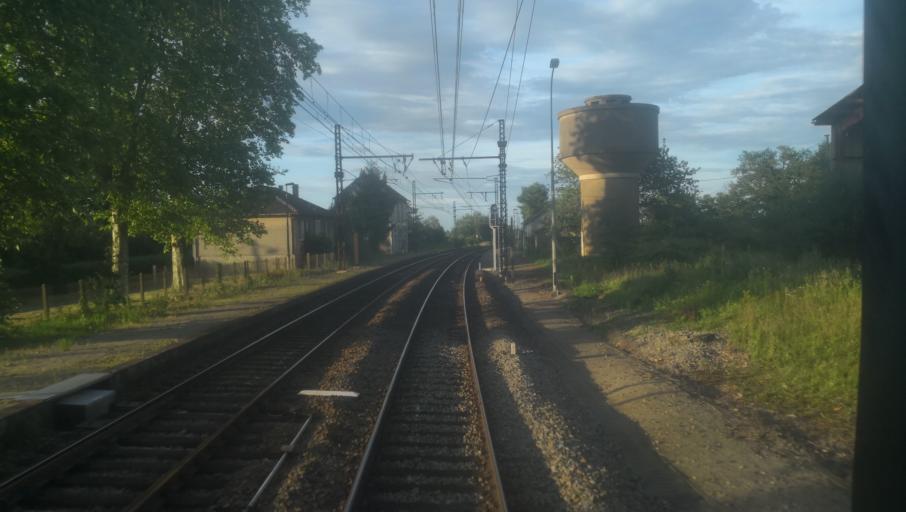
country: FR
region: Centre
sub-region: Departement de l'Indre
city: Le Pechereau
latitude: 46.5166
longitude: 1.5023
